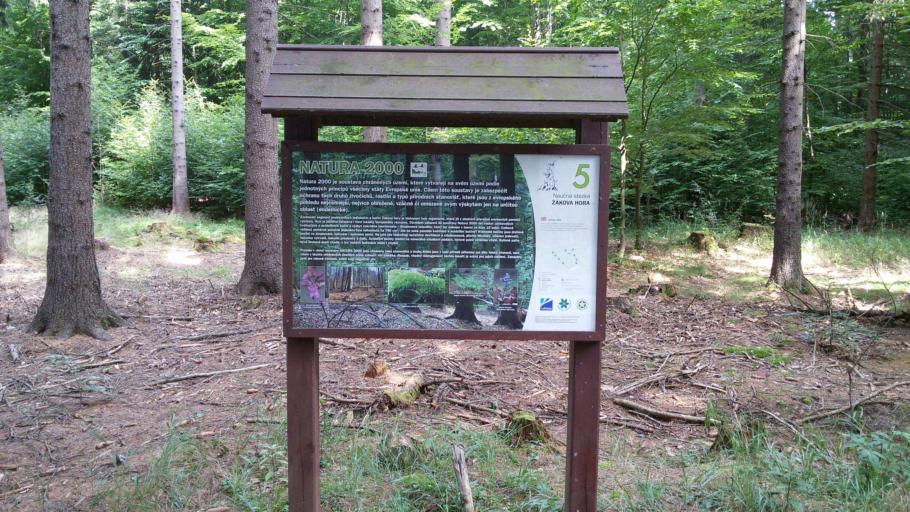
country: CZ
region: Vysocina
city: Heralec
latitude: 49.6523
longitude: 15.9967
